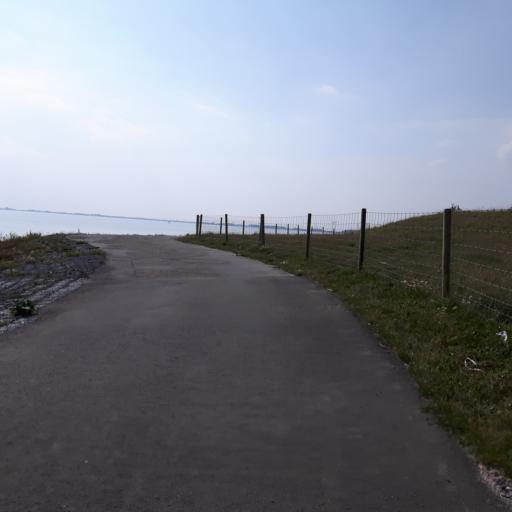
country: NL
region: Zeeland
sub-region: Gemeente Reimerswaal
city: Yerseke
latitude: 51.4537
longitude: 3.9882
